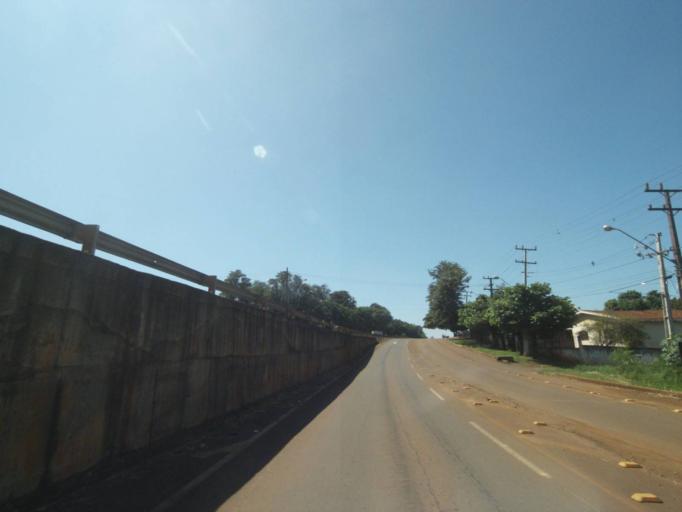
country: BR
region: Parana
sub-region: Londrina
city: Londrina
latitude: -23.3729
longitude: -51.1390
